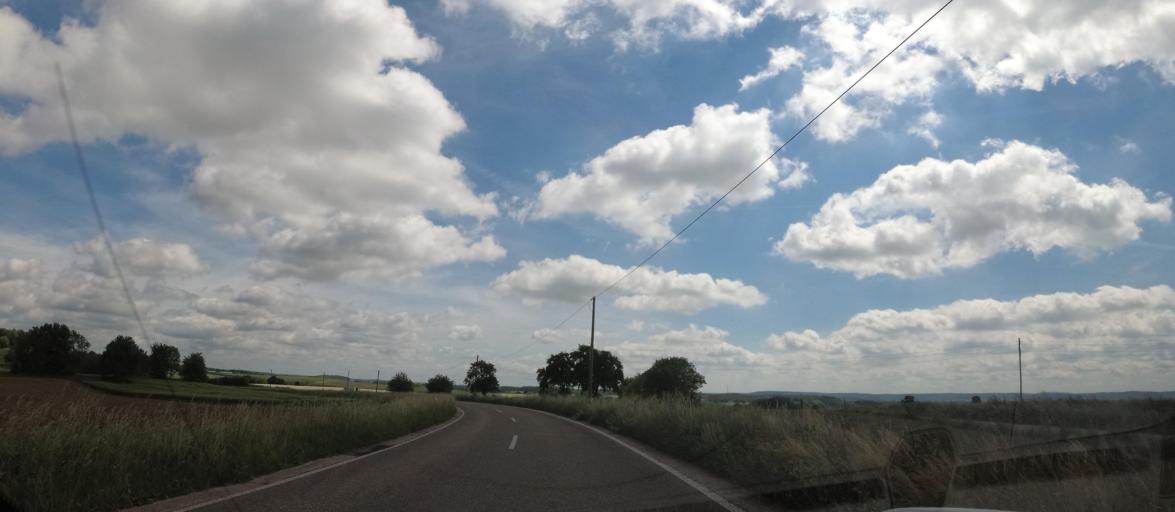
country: DE
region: Baden-Wuerttemberg
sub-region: Karlsruhe Region
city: Zaisenhausen
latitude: 49.1558
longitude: 8.8225
